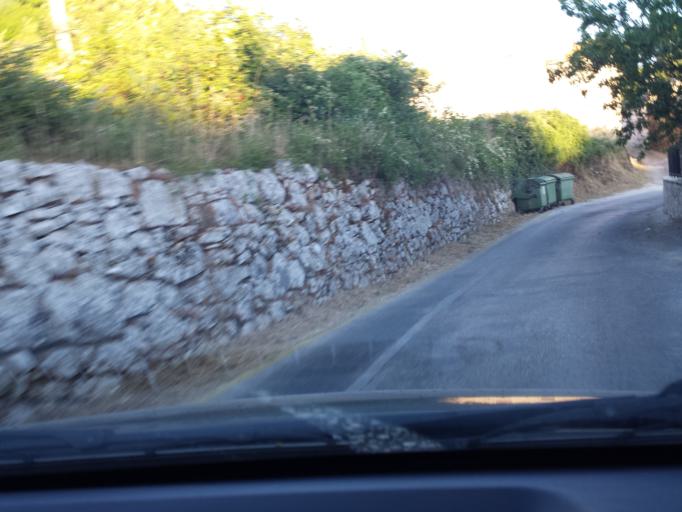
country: GR
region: Ionian Islands
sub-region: Nomos Kerkyras
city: Acharavi
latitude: 39.7447
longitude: 19.8371
